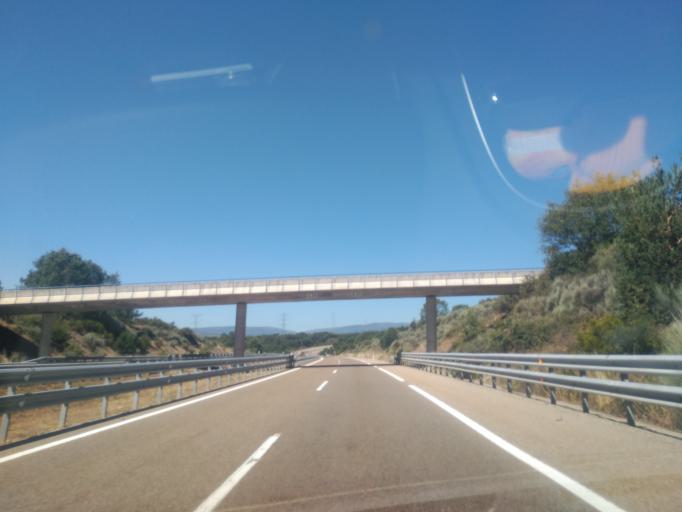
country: ES
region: Castille and Leon
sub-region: Provincia de Zamora
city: Asturianos
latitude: 42.0458
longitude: -6.4988
